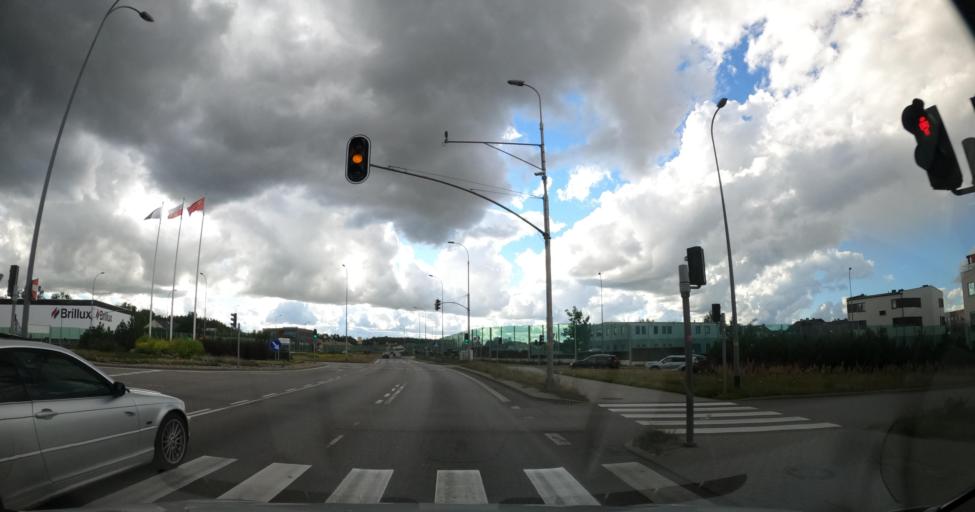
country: PL
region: Pomeranian Voivodeship
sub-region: Powiat gdanski
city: Kowale
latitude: 54.3502
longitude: 18.5114
